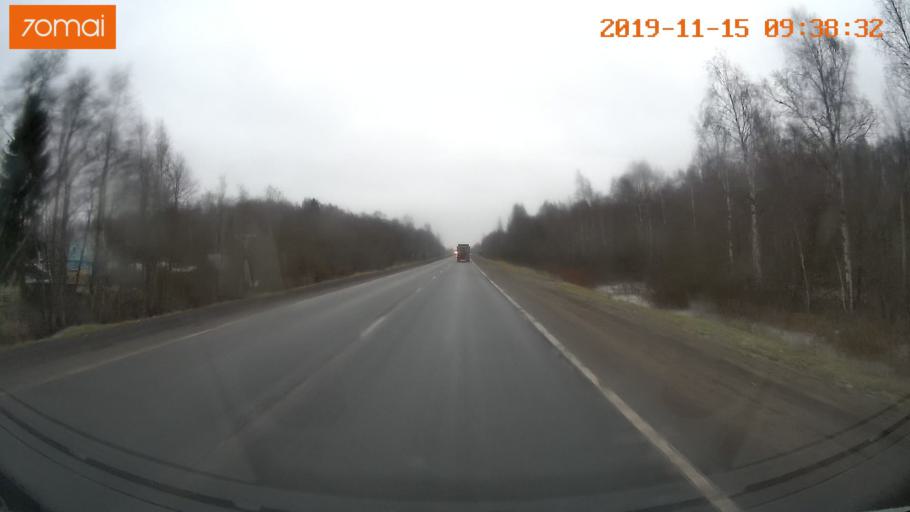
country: RU
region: Vologda
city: Sheksna
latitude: 59.2310
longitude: 38.4575
